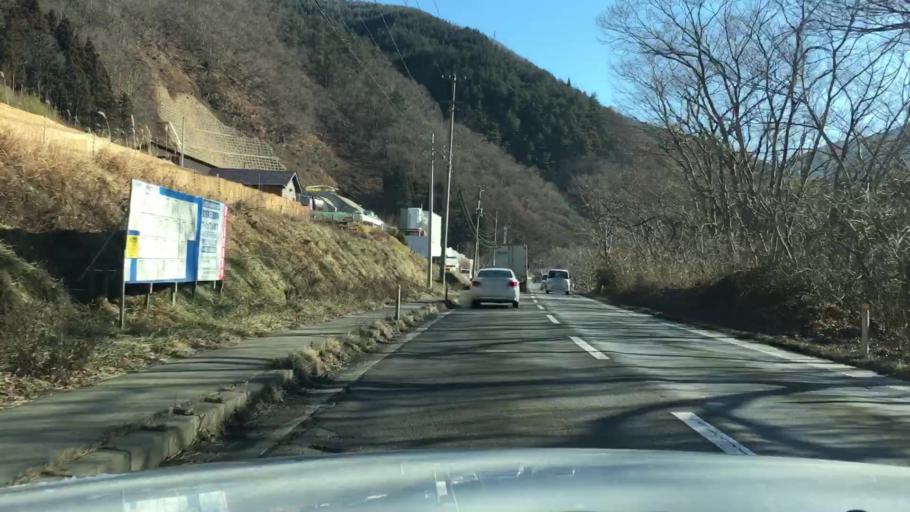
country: JP
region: Iwate
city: Miyako
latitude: 39.5966
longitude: 141.6532
